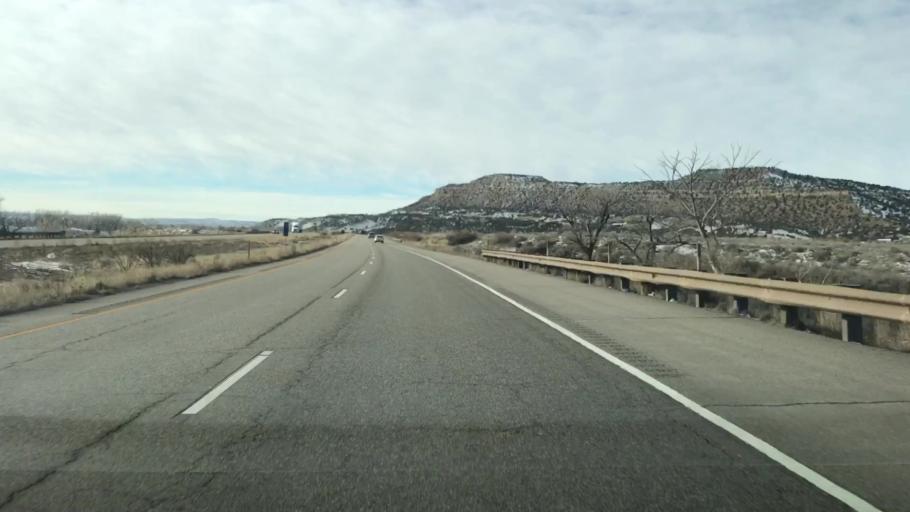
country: US
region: Colorado
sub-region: Garfield County
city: Parachute
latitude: 39.3504
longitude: -108.1818
